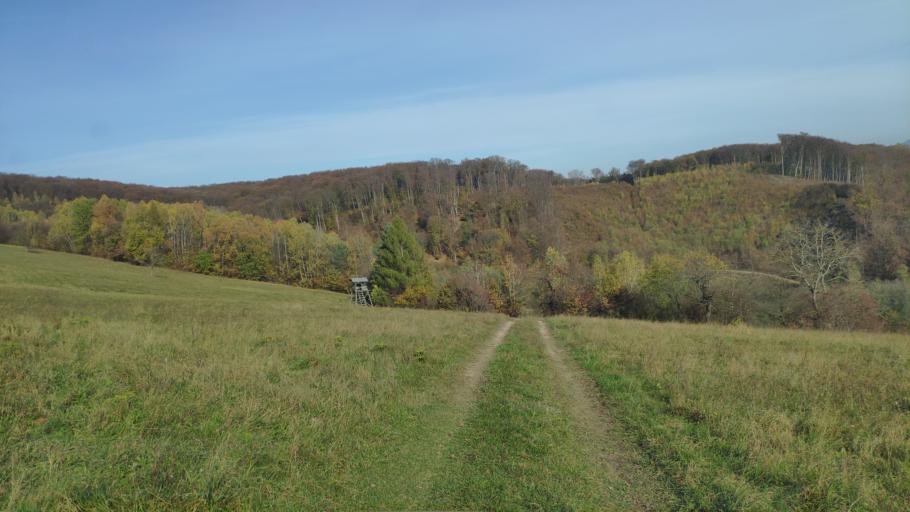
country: SK
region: Presovsky
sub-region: Okres Presov
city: Presov
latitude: 48.8998
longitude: 21.2219
